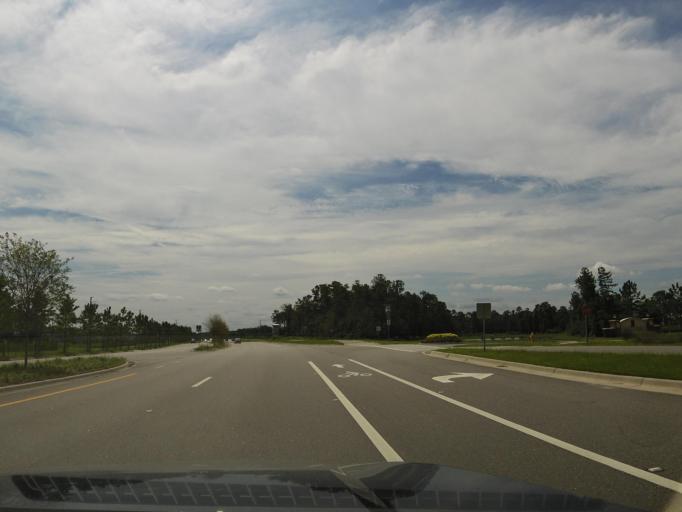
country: US
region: Florida
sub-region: Saint Johns County
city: Fruit Cove
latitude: 30.0419
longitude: -81.5293
